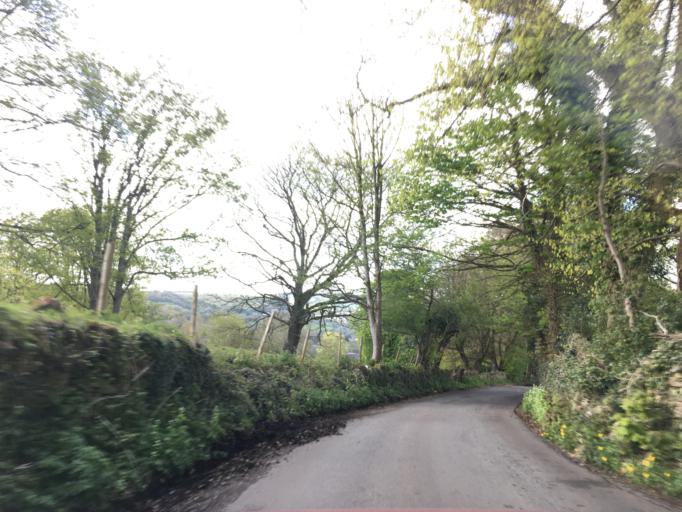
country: GB
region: England
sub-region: Gloucestershire
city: Brimscombe
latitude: 51.7140
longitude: -2.1946
